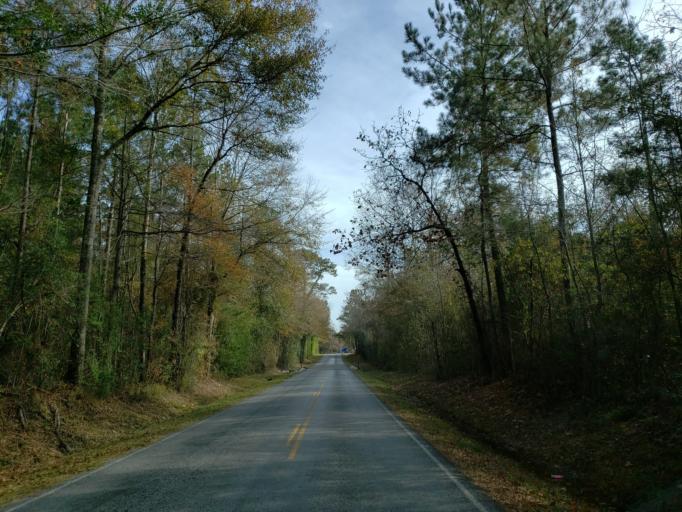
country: US
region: Mississippi
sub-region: Forrest County
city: Rawls Springs
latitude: 31.4022
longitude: -89.3958
